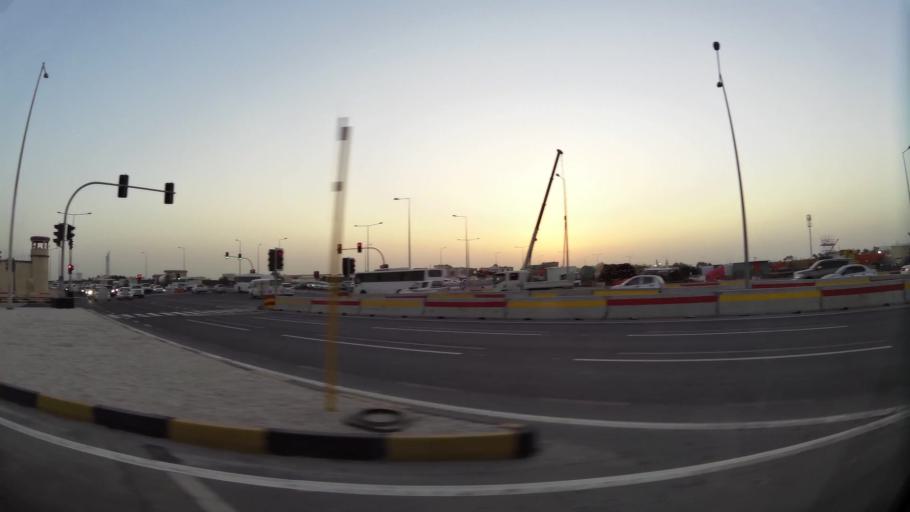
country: QA
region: Baladiyat ar Rayyan
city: Ar Rayyan
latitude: 25.2930
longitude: 51.4660
